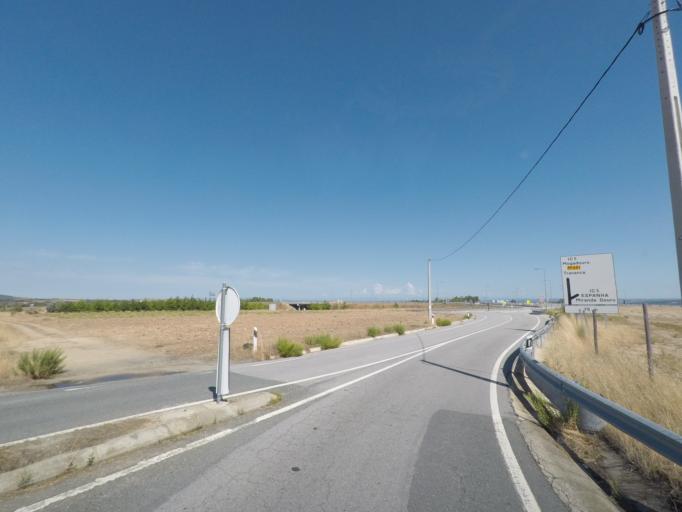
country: ES
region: Castille and Leon
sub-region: Provincia de Salamanca
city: Villarino de los Aires
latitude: 41.3666
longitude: -6.5051
